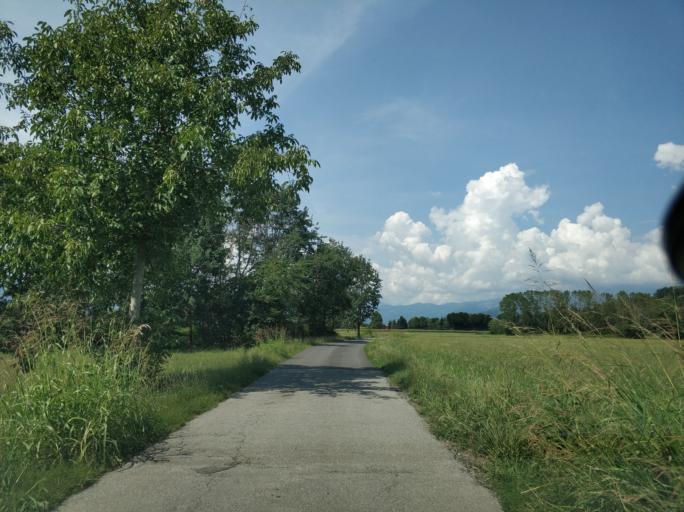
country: IT
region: Piedmont
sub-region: Provincia di Torino
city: San Carlo Canavese
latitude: 45.2362
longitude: 7.6205
